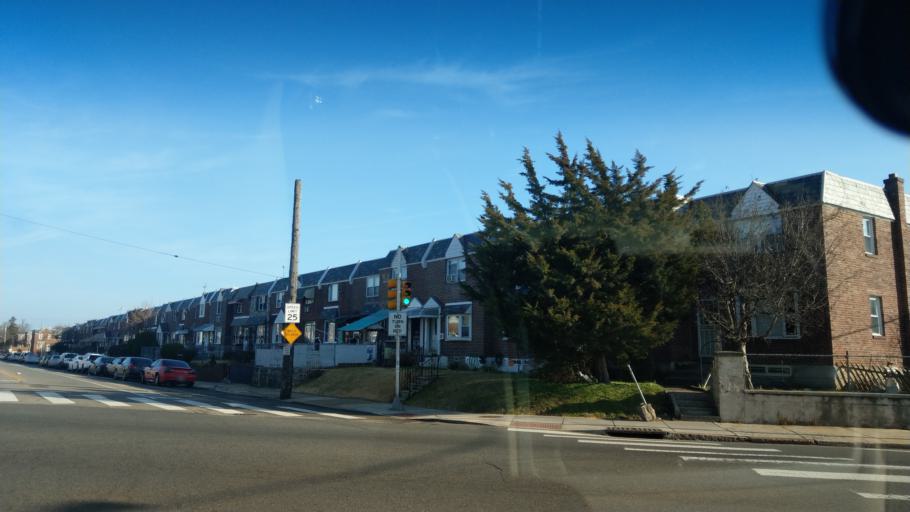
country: US
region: Pennsylvania
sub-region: Montgomery County
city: Rockledge
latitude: 40.0284
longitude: -75.1202
